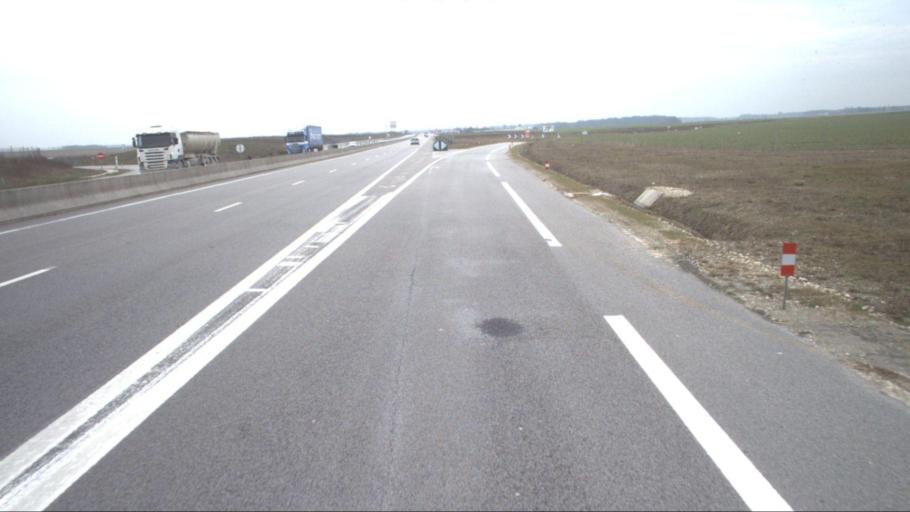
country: FR
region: Ile-de-France
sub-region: Departement des Yvelines
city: Sonchamp
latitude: 48.5823
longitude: 1.8321
